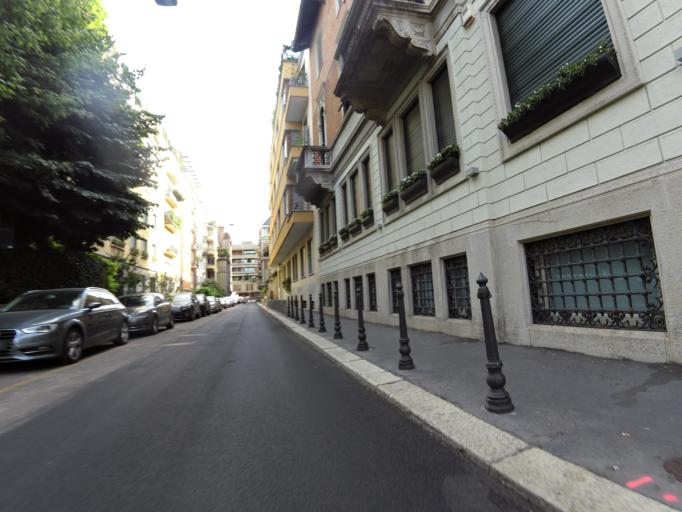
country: IT
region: Lombardy
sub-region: Citta metropolitana di Milano
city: Milano
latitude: 45.4639
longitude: 9.1730
